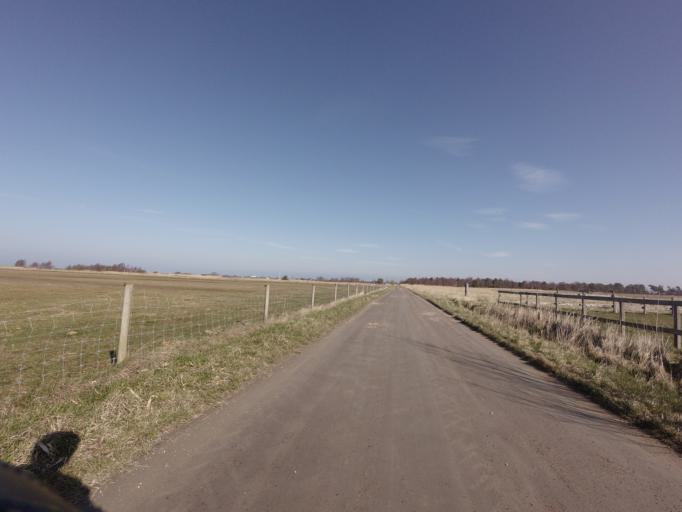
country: SE
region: Skane
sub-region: Vellinge Kommun
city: Skanor med Falsterbo
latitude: 55.4292
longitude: 12.8584
